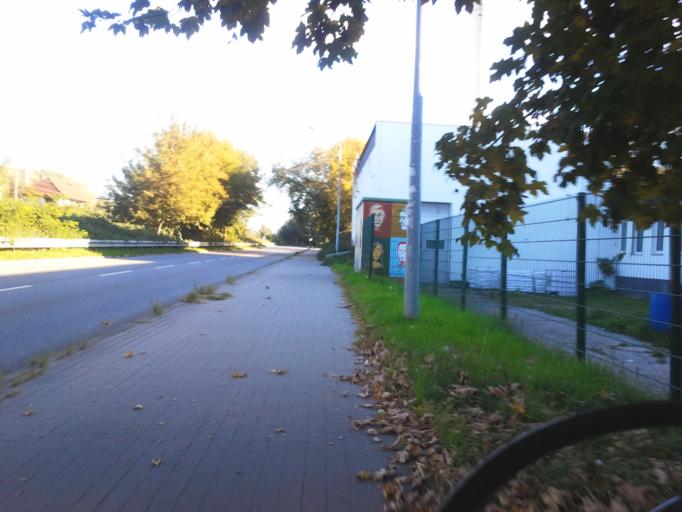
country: DE
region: Mecklenburg-Vorpommern
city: Rostock
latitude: 54.1078
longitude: 12.0839
